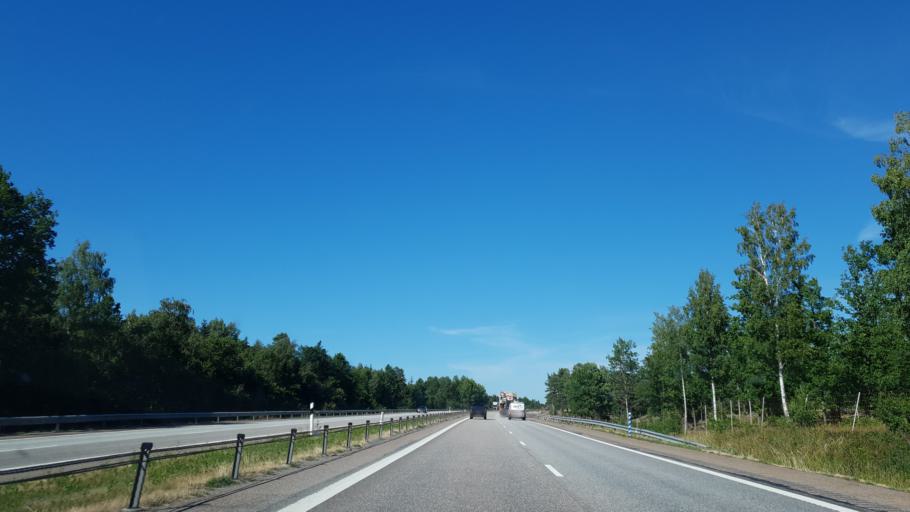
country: SE
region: OEstergoetland
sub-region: Odeshogs Kommun
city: OEdeshoeg
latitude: 58.1913
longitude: 14.6085
